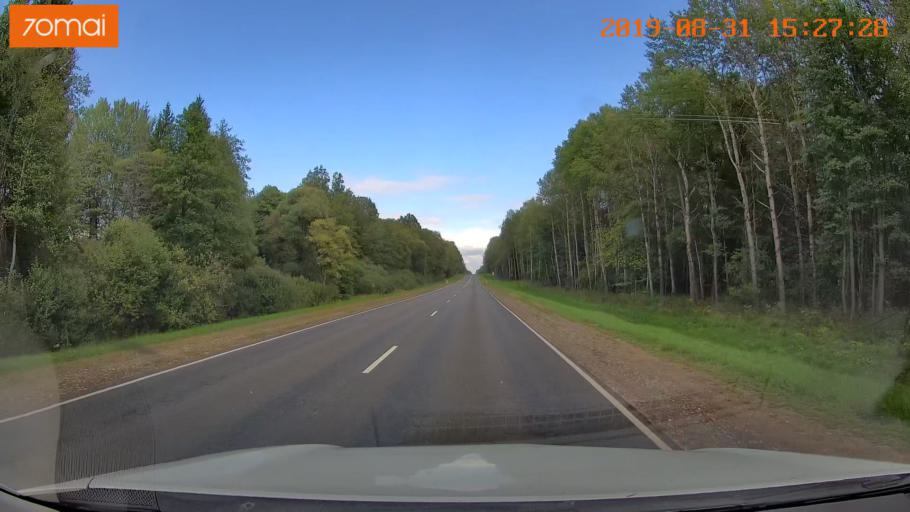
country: RU
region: Kaluga
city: Baryatino
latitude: 54.5557
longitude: 34.5579
